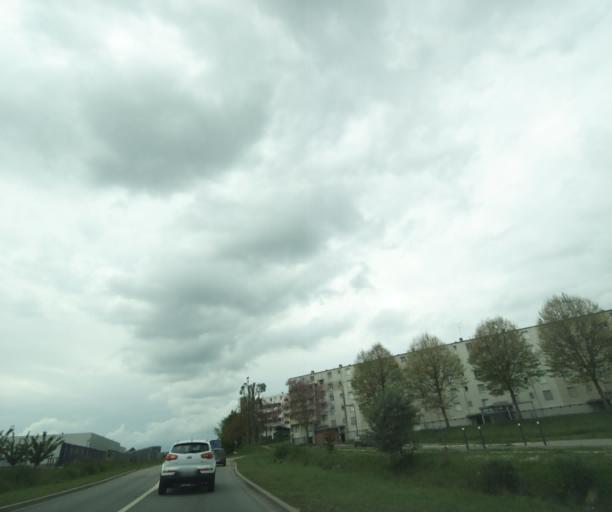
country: FR
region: Ile-de-France
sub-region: Departement des Yvelines
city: Ecquevilly
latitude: 48.9491
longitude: 1.9283
